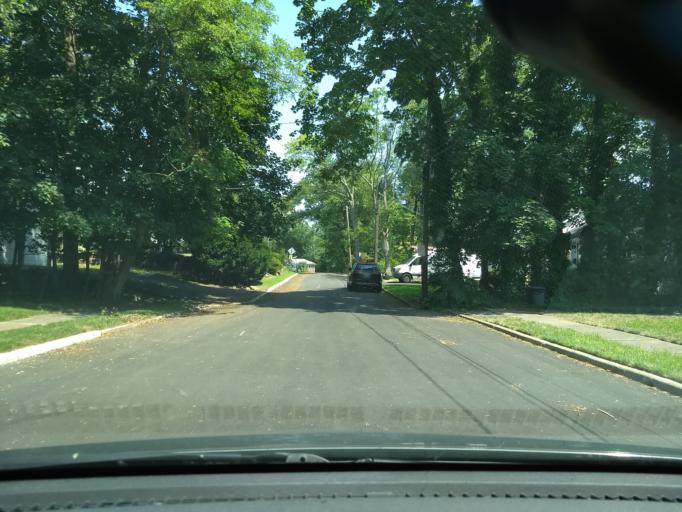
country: US
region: New Jersey
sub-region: Bergen County
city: Ridgewood
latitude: 40.9757
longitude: -74.1092
